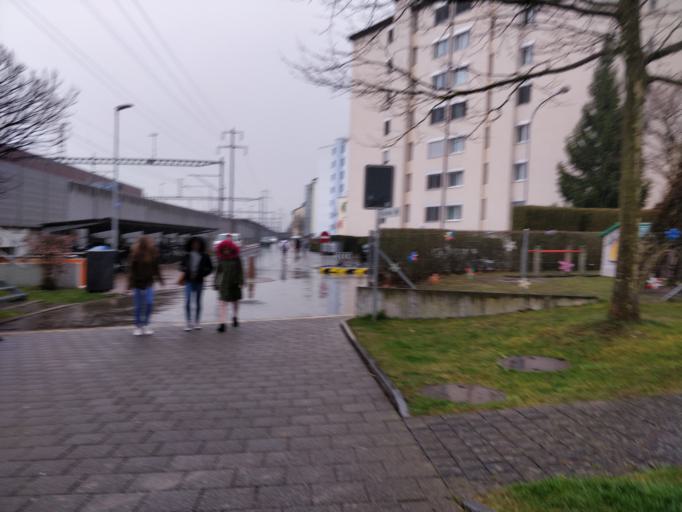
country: CH
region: Zurich
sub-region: Bezirk Uster
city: Schwerzenbach / Chimli
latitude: 47.3853
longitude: 8.6562
